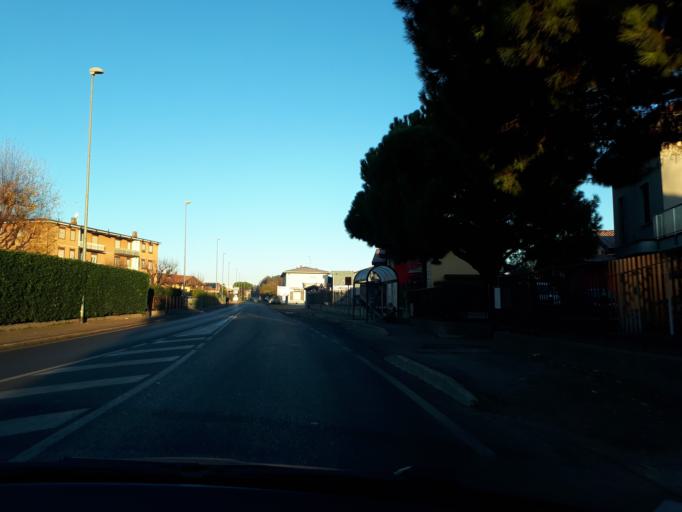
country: IT
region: Lombardy
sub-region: Provincia di Como
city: Bulgorello
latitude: 45.7344
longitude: 9.0594
